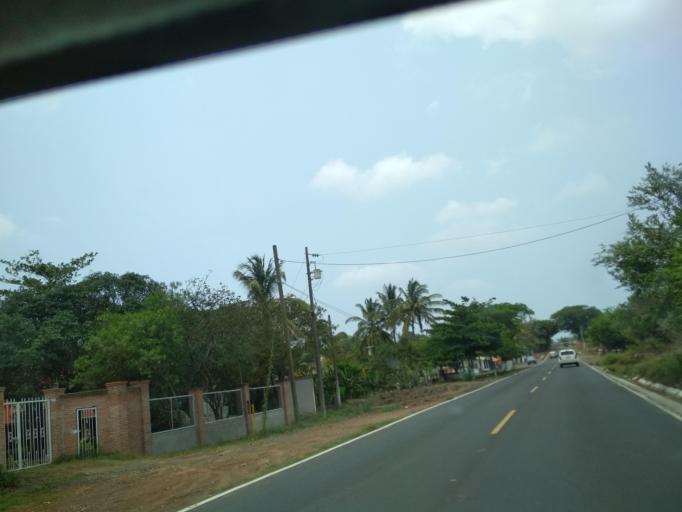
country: MX
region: Veracruz
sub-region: Veracruz
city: Delfino Victoria (Santa Fe)
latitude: 19.1723
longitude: -96.2775
